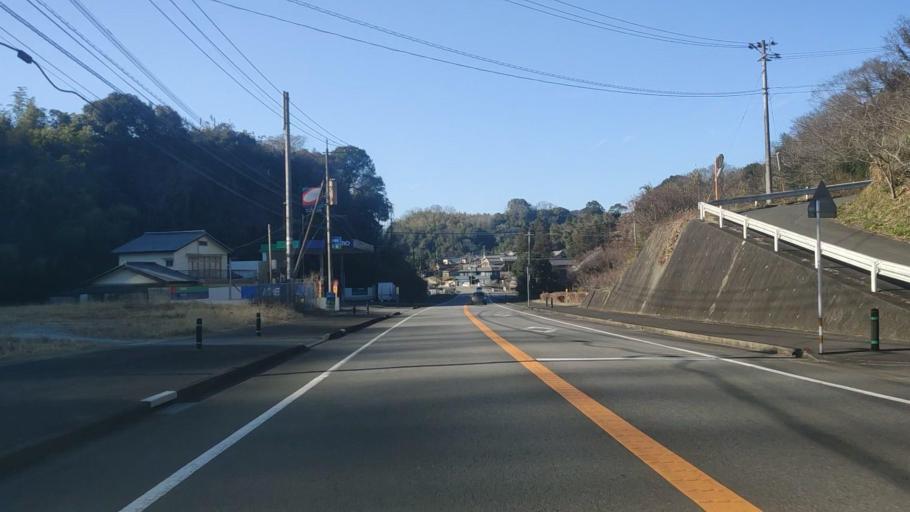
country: JP
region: Oita
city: Usuki
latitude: 33.0633
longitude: 131.6639
